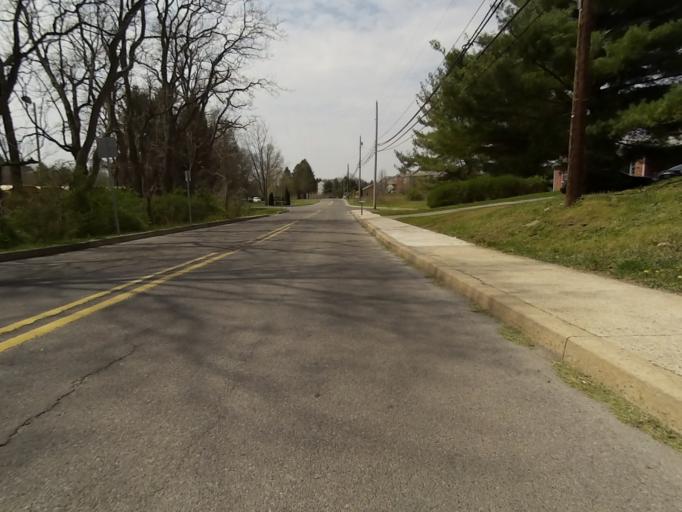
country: US
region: Pennsylvania
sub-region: Centre County
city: State College
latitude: 40.8005
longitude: -77.8835
